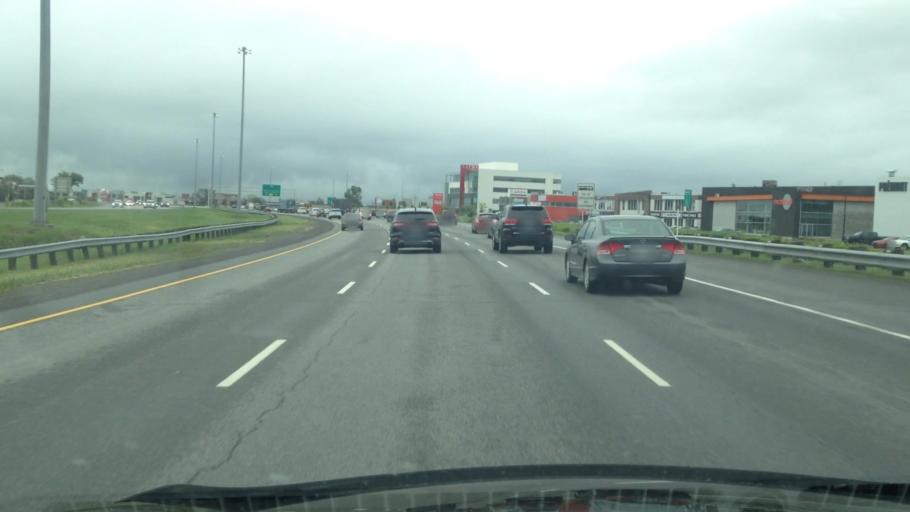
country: CA
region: Quebec
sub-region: Laurentides
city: Rosemere
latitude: 45.5796
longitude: -73.7694
